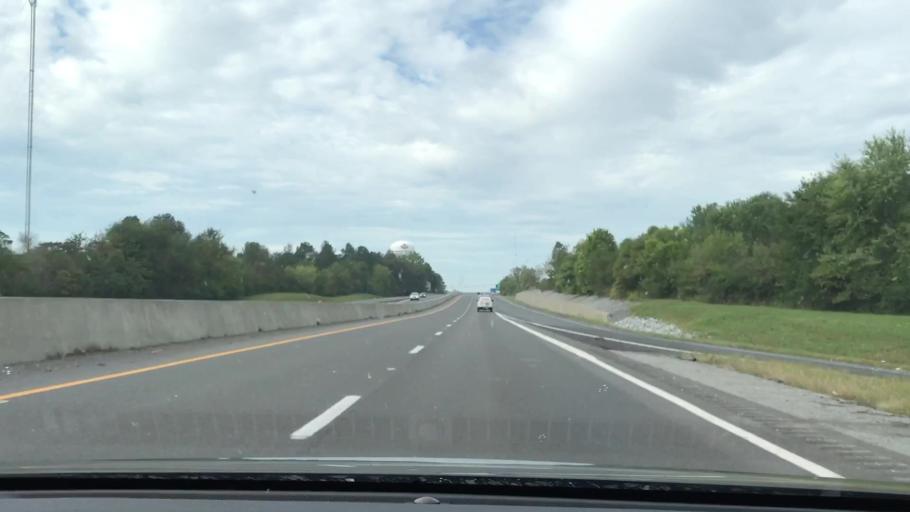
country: US
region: Kentucky
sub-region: Graves County
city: Mayfield
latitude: 36.7663
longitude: -88.6443
